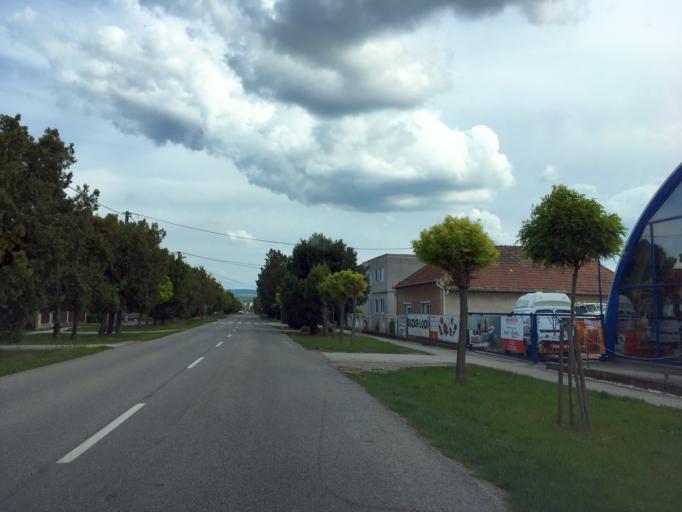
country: HU
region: Komarom-Esztergom
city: Dunaalmas
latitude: 47.7546
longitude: 18.3209
